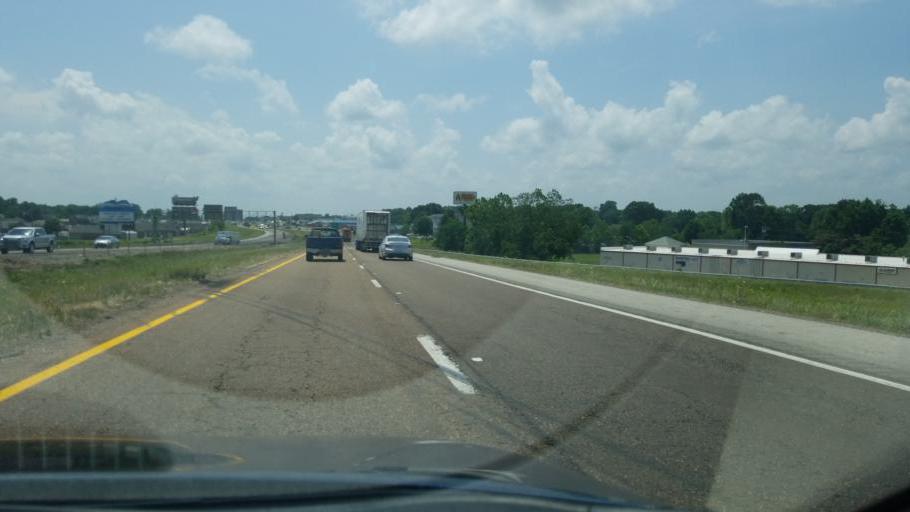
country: US
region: Tennessee
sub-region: Madison County
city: Jackson
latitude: 35.6707
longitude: -88.8309
